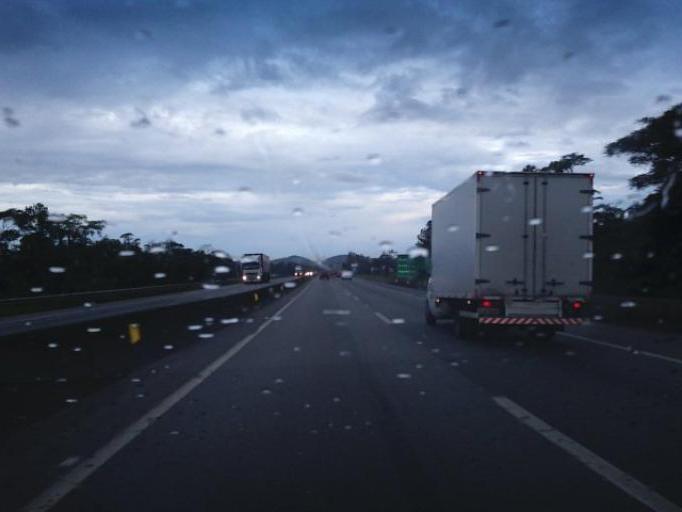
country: BR
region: Santa Catarina
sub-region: Joinville
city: Joinville
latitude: -26.0312
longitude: -48.8608
